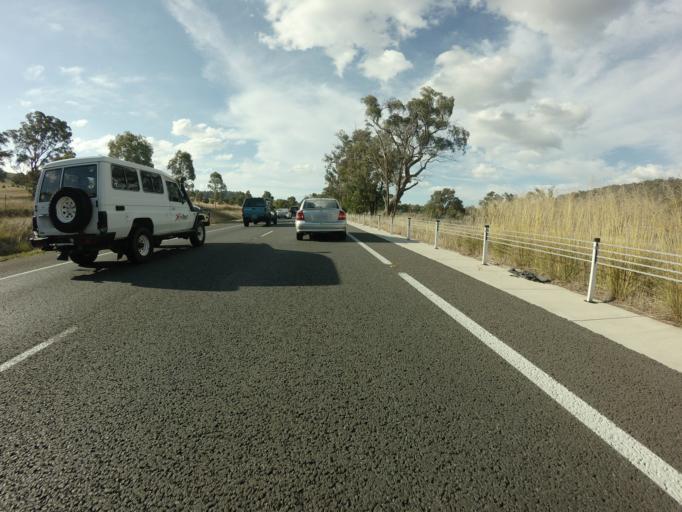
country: AU
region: Australian Capital Territory
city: Kaleen
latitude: -35.2215
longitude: 149.1958
